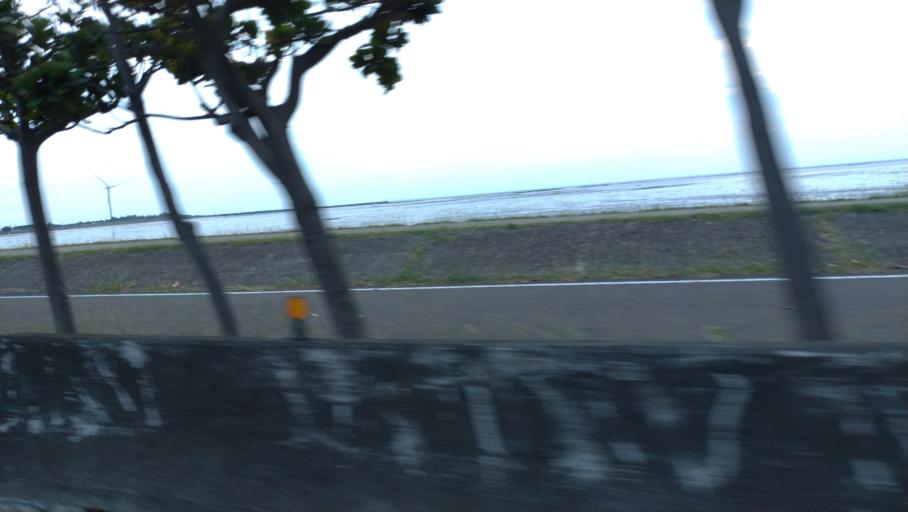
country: TW
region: Taiwan
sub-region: Hsinchu
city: Hsinchu
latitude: 24.7713
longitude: 120.9137
